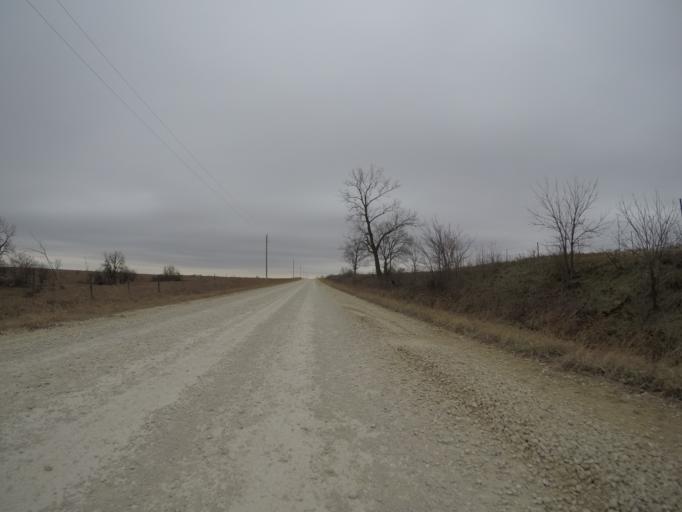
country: US
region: Kansas
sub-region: Wabaunsee County
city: Alma
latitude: 38.8365
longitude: -96.1133
